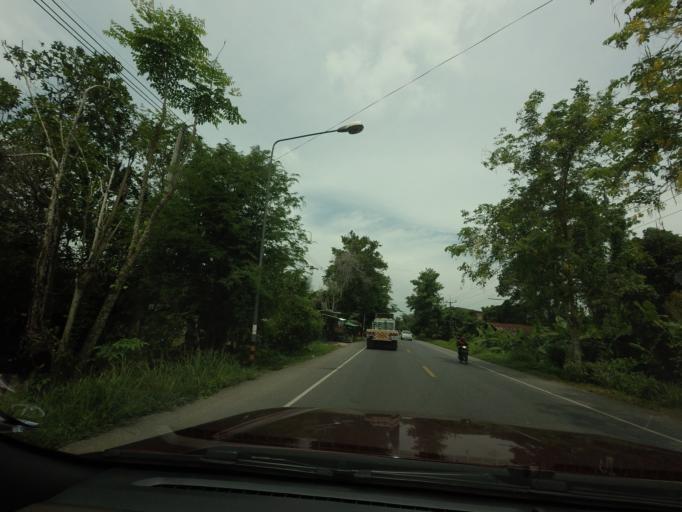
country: TH
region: Pattani
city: Mae Lan
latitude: 6.6582
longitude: 101.3039
